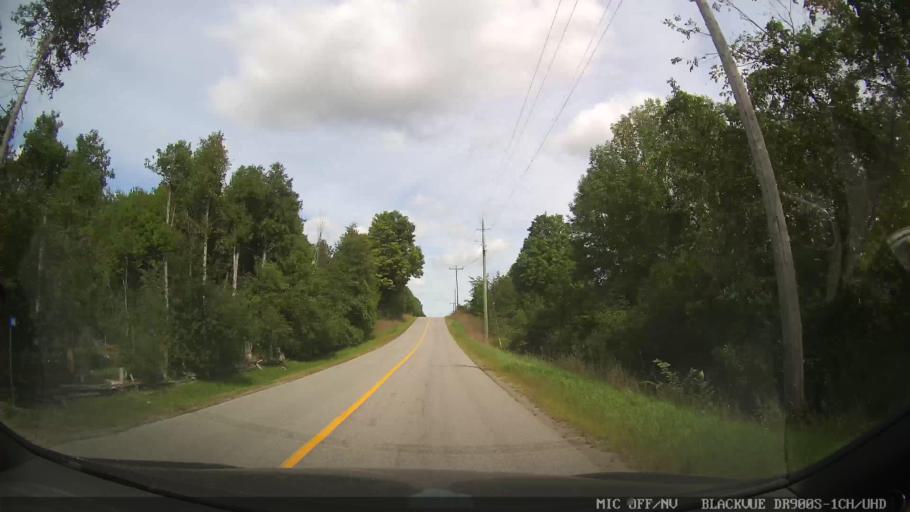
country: CA
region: Ontario
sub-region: Lanark County
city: Smiths Falls
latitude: 44.9063
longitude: -75.9014
